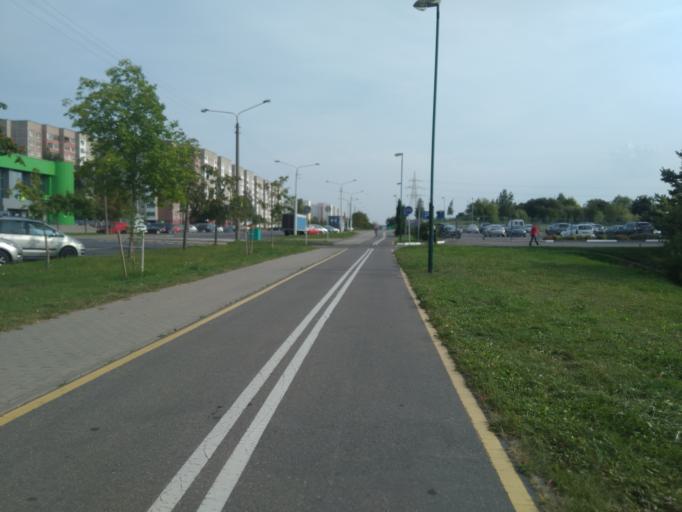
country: BY
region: Minsk
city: Minsk
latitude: 53.8622
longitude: 27.5872
